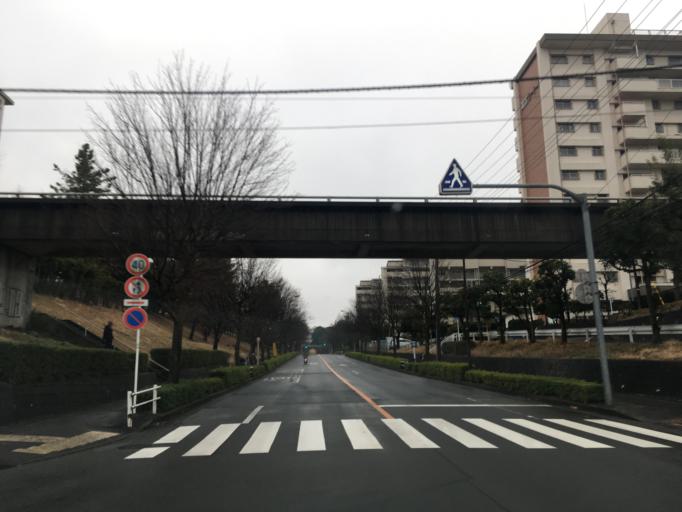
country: JP
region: Tokyo
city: Hino
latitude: 35.6263
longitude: 139.4552
